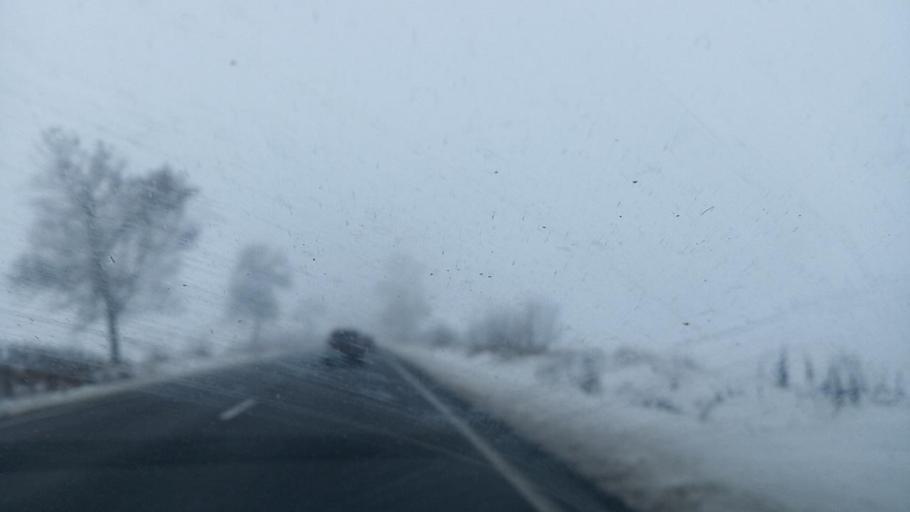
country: RO
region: Iasi
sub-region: Comuna Motca
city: Boureni
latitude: 47.1993
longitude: 26.6174
